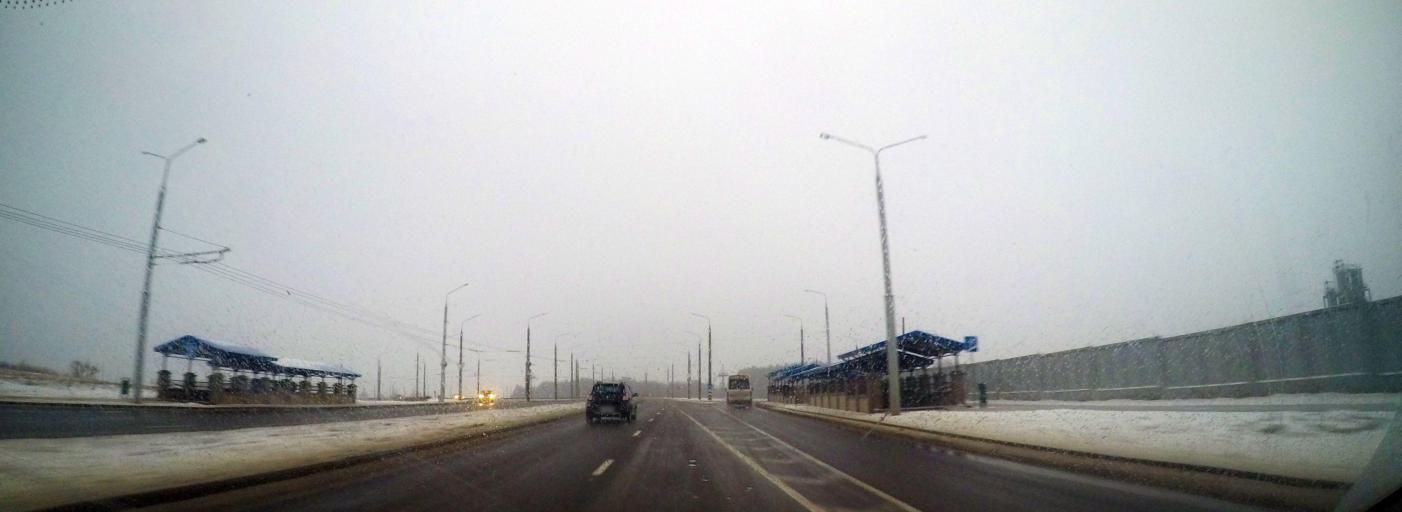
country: BY
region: Grodnenskaya
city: Hrodna
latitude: 53.6435
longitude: 23.8178
